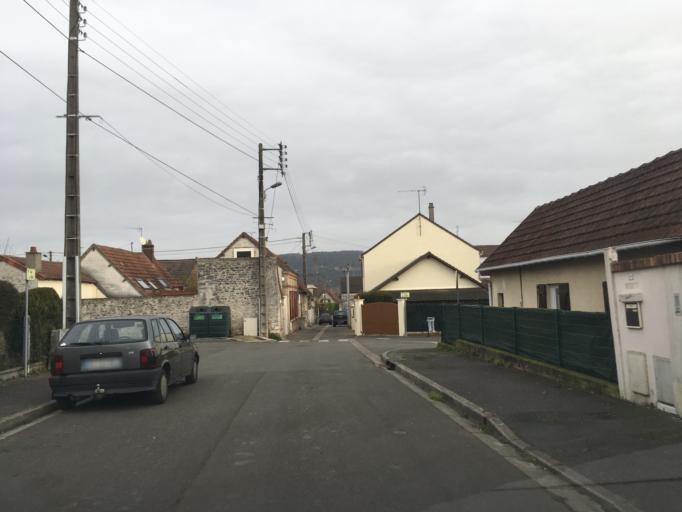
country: FR
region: Haute-Normandie
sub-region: Departement de l'Eure
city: Vernon
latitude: 49.0841
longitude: 1.4917
